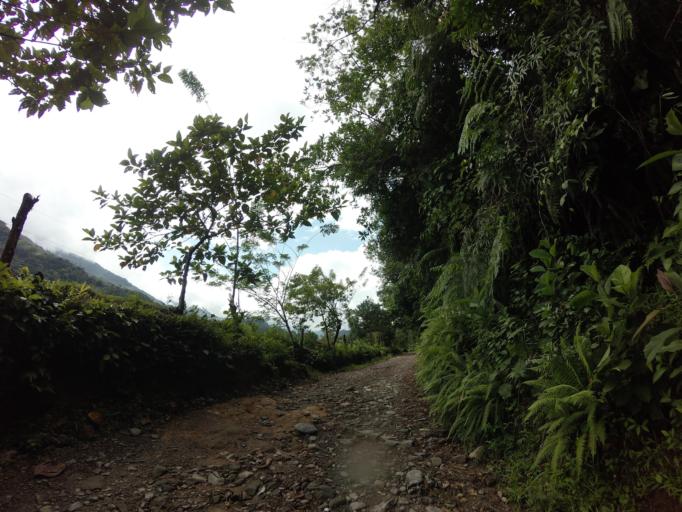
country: CO
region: Antioquia
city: Narino
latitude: 5.5317
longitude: -75.1366
